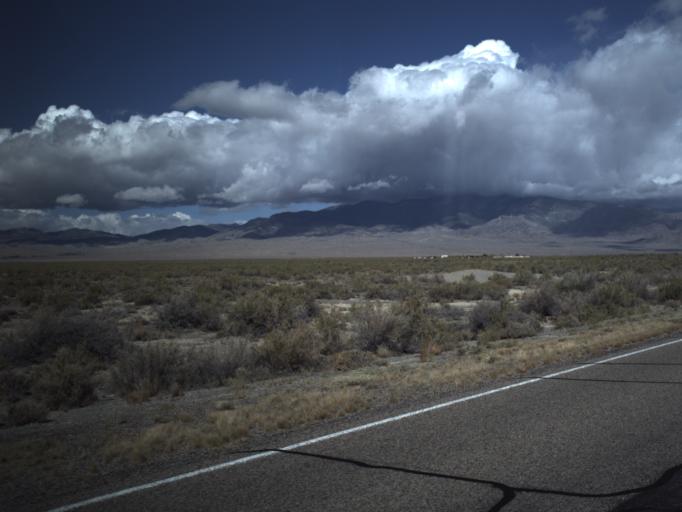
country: US
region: Nevada
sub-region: White Pine County
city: McGill
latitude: 39.0378
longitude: -114.0360
